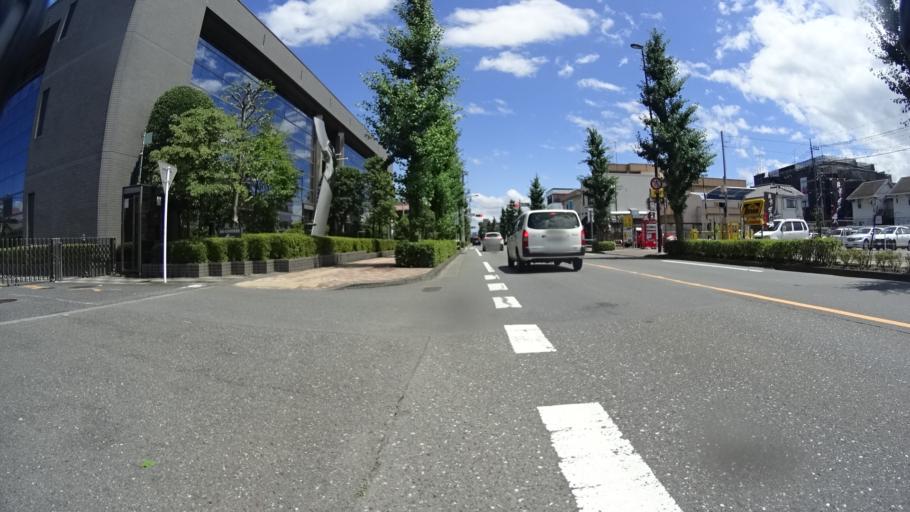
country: JP
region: Tokyo
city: Ome
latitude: 35.7800
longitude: 139.2891
